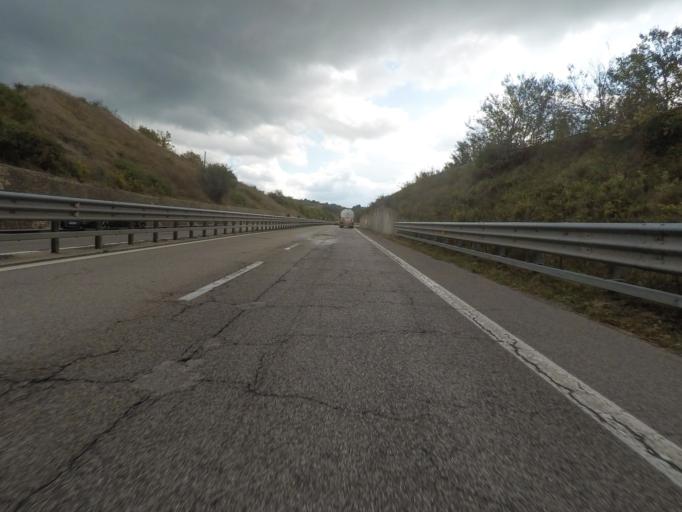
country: IT
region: Tuscany
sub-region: Provincia di Siena
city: Rapolano Terme
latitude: 43.3103
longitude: 11.5833
